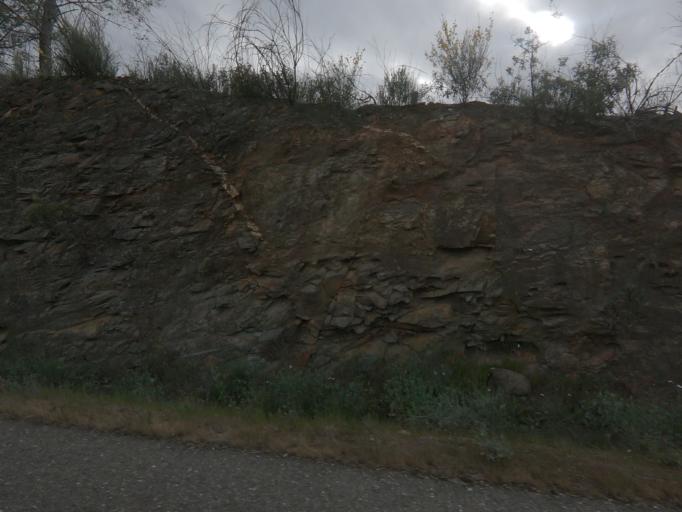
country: ES
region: Extremadura
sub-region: Provincia de Caceres
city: Acebo
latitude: 40.2078
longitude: -6.6756
